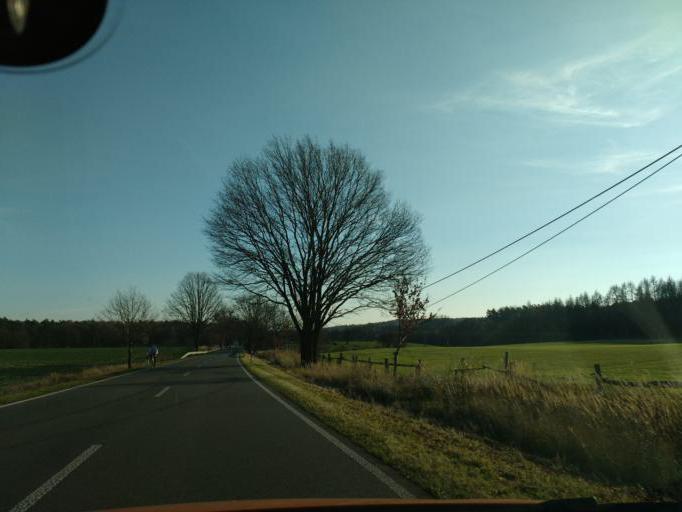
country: DE
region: Brandenburg
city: Protzel
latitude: 52.6433
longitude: 13.9672
